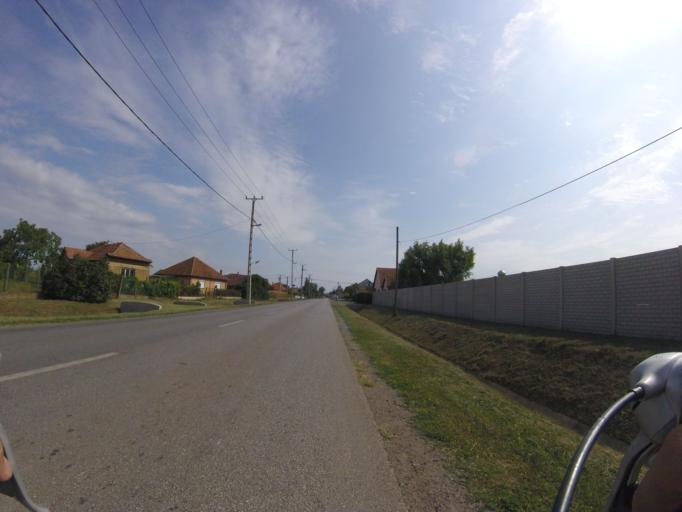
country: HU
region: Szabolcs-Szatmar-Bereg
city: Kemecse
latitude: 48.0657
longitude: 21.7959
